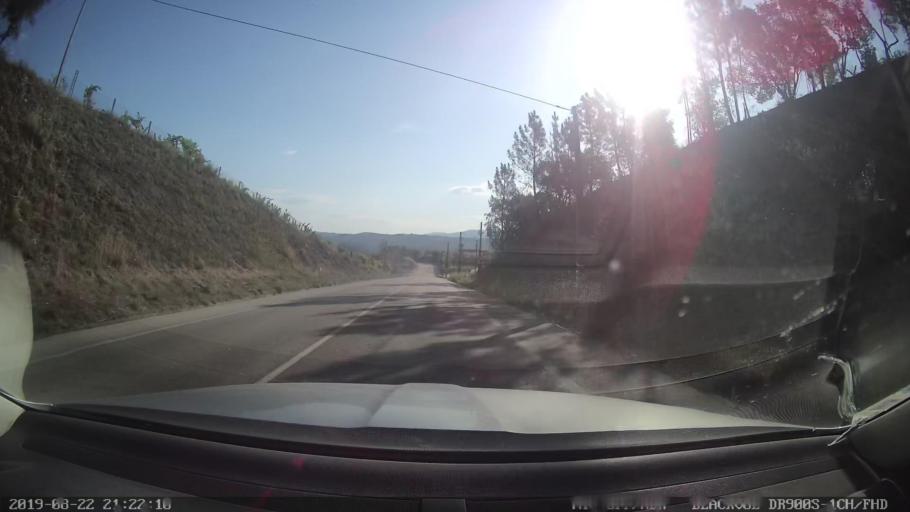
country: PT
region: Castelo Branco
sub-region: Serta
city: Serta
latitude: 39.8200
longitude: -8.1039
